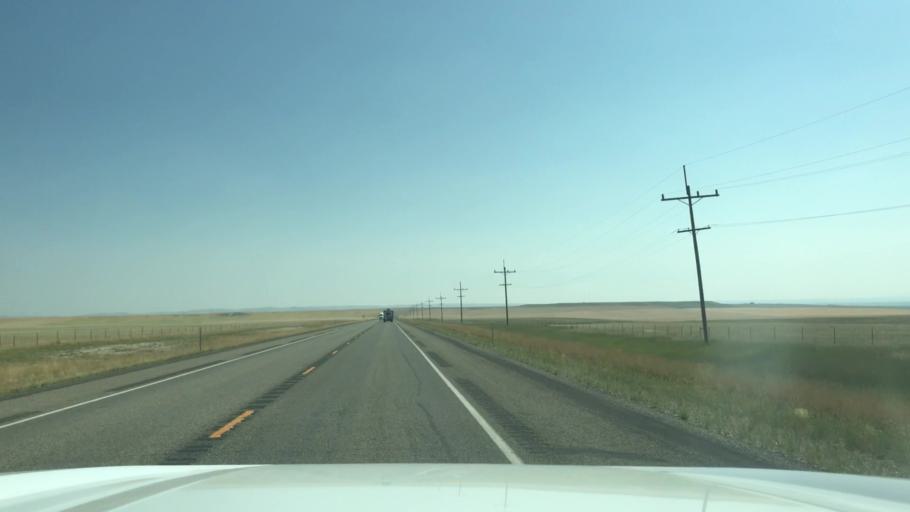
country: US
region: Montana
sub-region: Wheatland County
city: Harlowton
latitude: 46.5004
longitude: -109.7661
